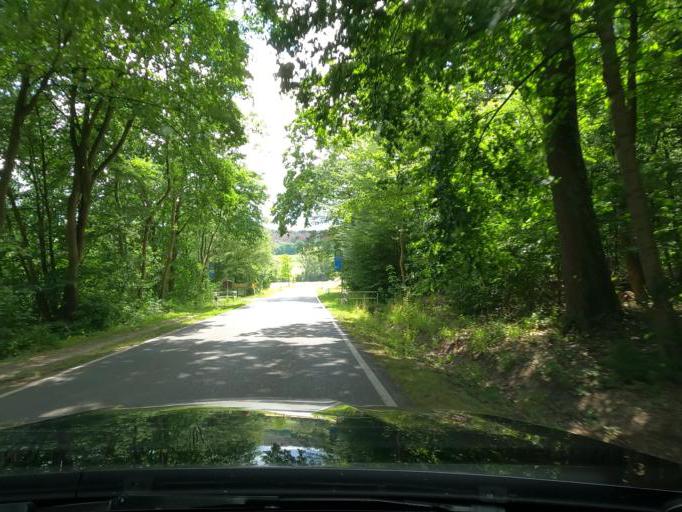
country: DE
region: Lower Saxony
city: Elbe
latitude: 52.1165
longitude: 10.2876
